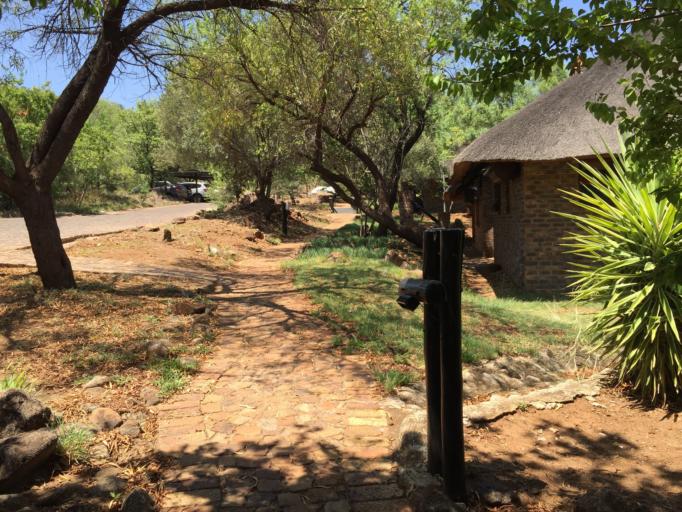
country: ZA
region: North-West
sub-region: Bojanala Platinum District Municipality
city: Mogwase
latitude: -25.3415
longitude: 27.0578
